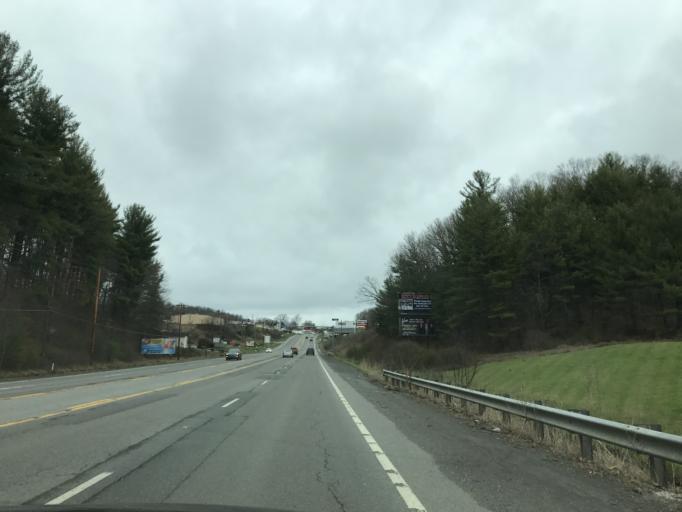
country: US
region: West Virginia
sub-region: Raleigh County
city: Crab Orchard
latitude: 37.7485
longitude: -81.2221
